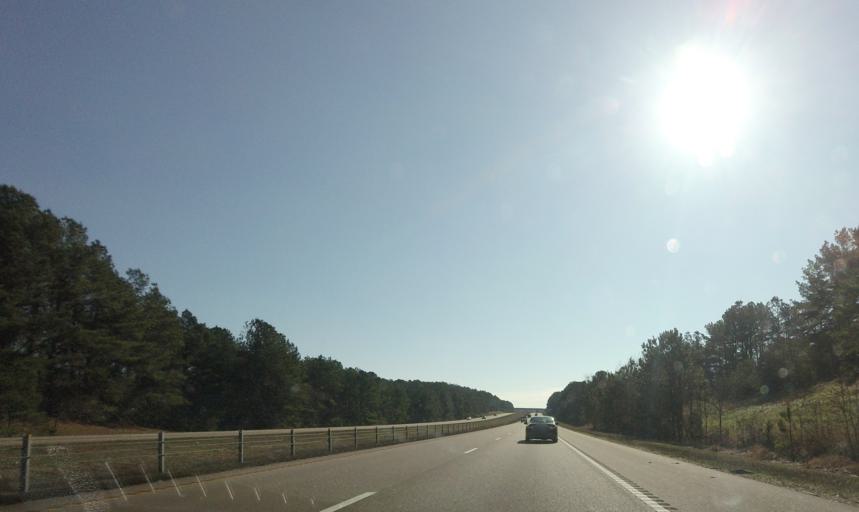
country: US
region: Mississippi
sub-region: Marshall County
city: Holly Springs
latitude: 34.7669
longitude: -89.4687
